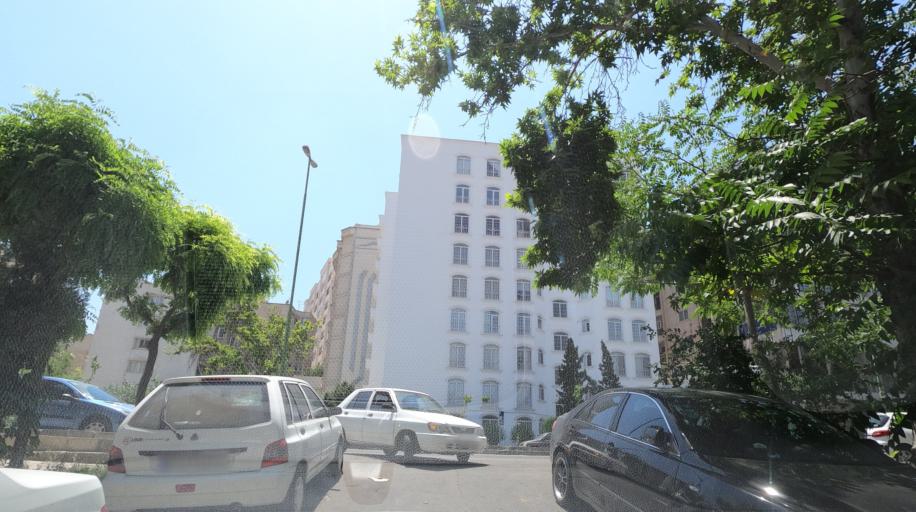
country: IR
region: Tehran
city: Tajrish
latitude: 35.7866
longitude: 51.3842
